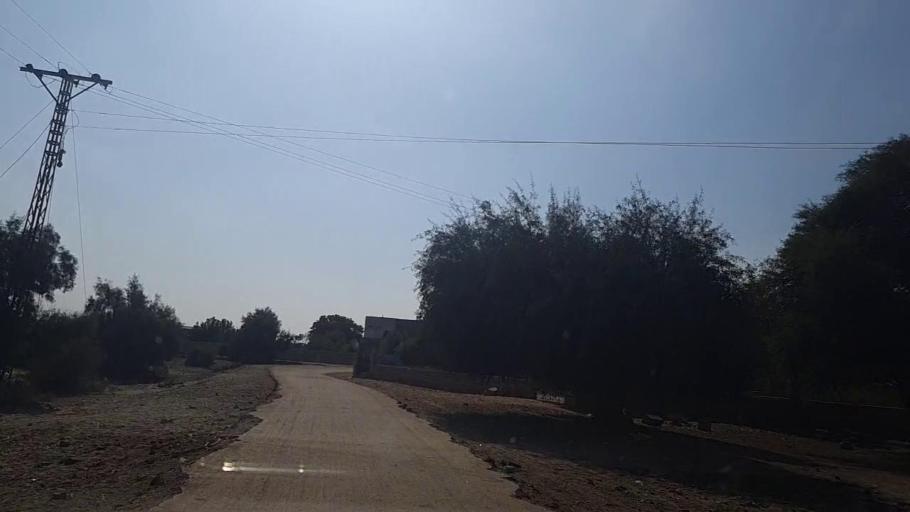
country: PK
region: Sindh
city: Sehwan
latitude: 26.2733
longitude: 68.0354
